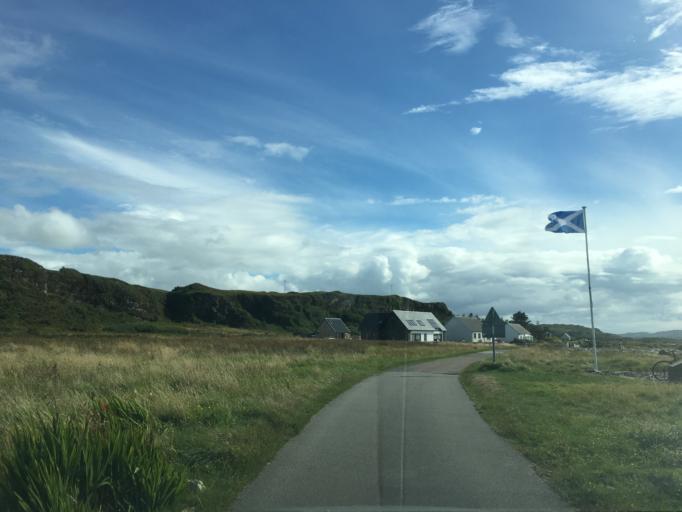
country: GB
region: Scotland
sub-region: Argyll and Bute
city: Isle Of Mull
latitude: 56.2554
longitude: -5.6535
